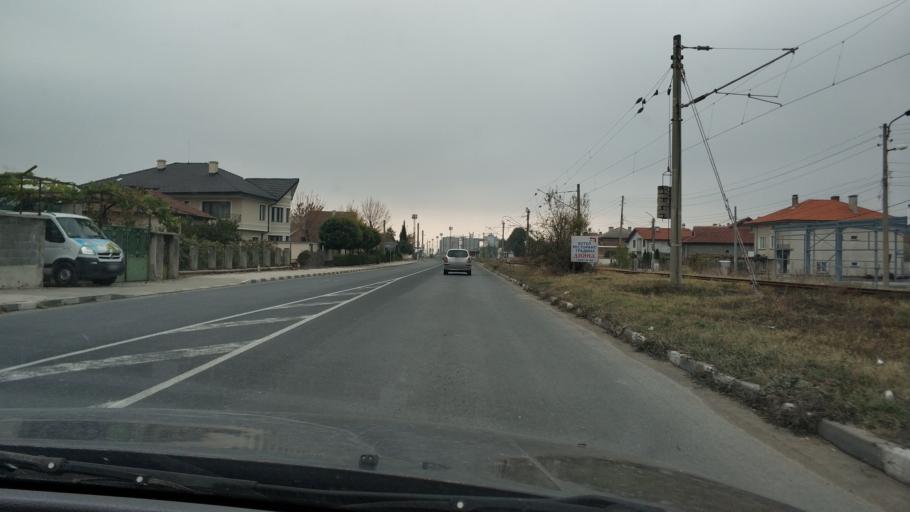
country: BG
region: Plovdiv
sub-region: Obshtina Plovdiv
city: Plovdiv
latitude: 42.2359
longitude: 24.7235
